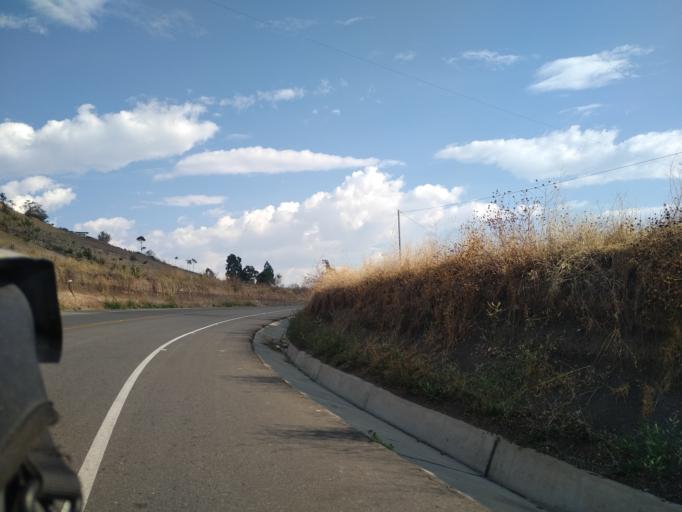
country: PE
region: Cajamarca
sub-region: San Marcos
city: San Marcos
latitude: -7.3801
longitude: -78.1252
